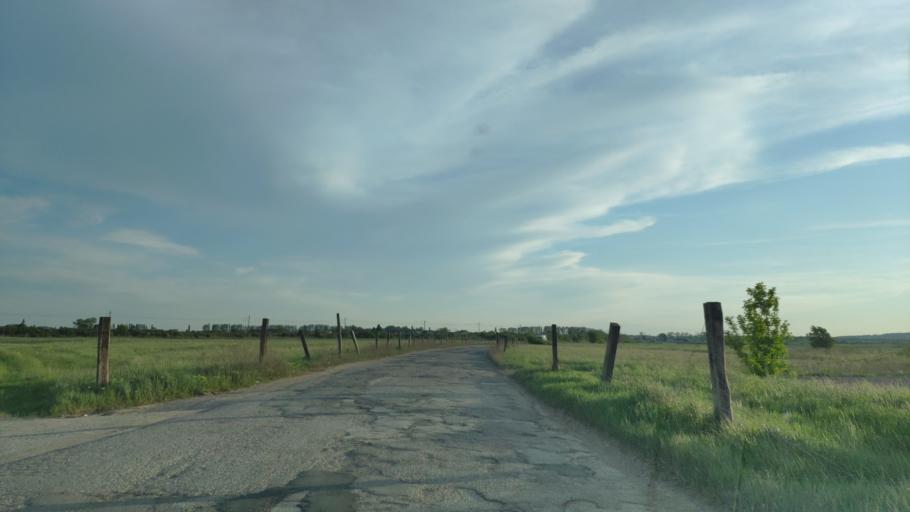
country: SK
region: Kosicky
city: Kosice
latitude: 48.6532
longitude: 21.3062
